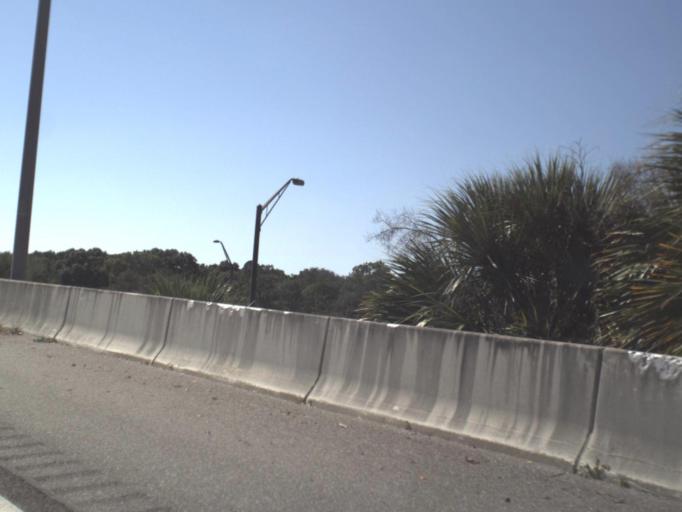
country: US
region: Florida
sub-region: Hillsborough County
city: Greater Northdale
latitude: 28.1228
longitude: -82.5459
